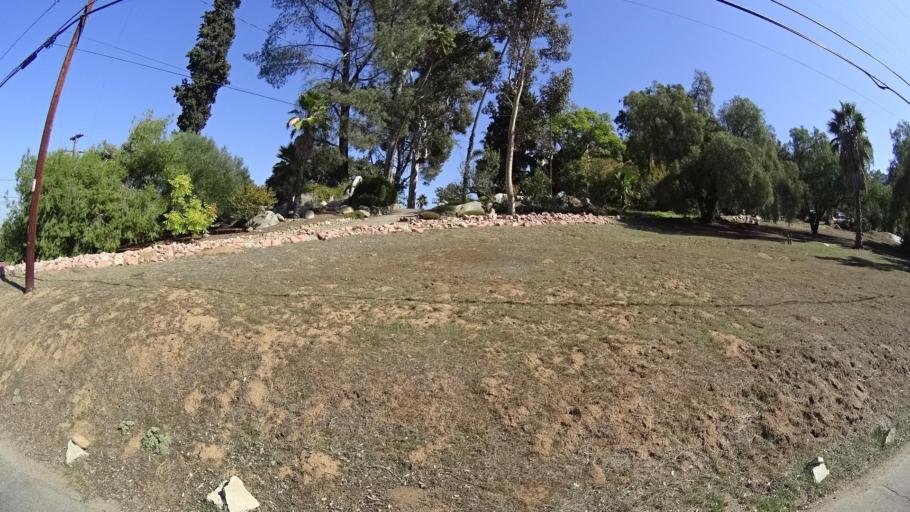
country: US
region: California
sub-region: San Diego County
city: El Cajon
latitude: 32.7779
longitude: -116.9510
